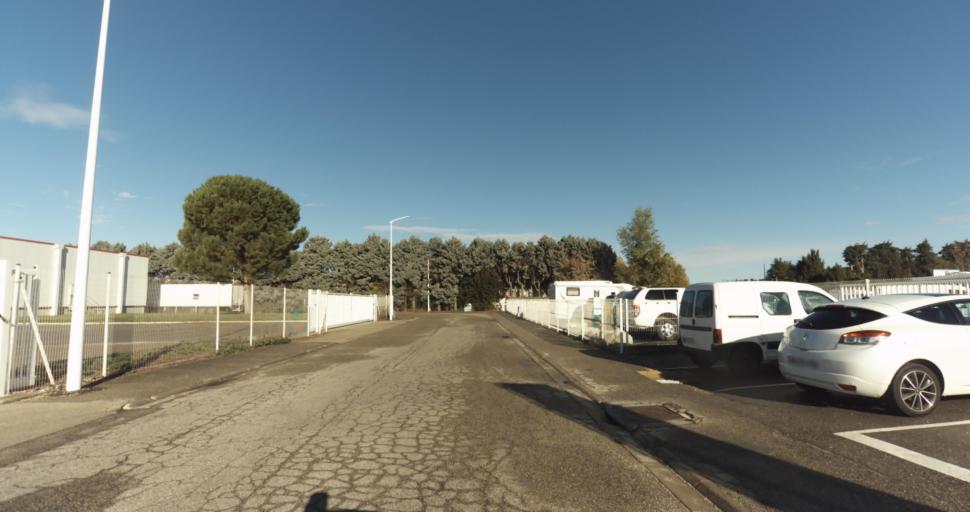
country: FR
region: Provence-Alpes-Cote d'Azur
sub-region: Departement des Bouches-du-Rhone
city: Rognonas
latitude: 43.8974
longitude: 4.8172
